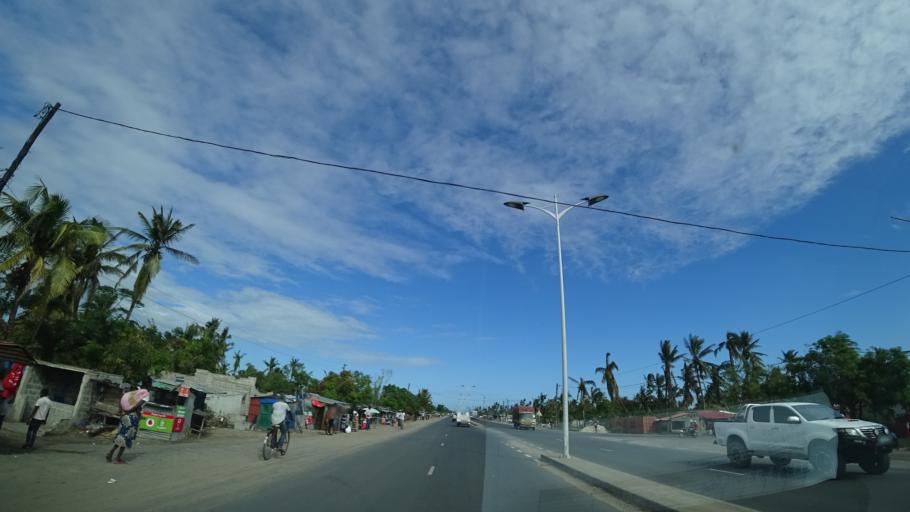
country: MZ
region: Sofala
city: Beira
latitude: -19.7601
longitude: 34.8790
